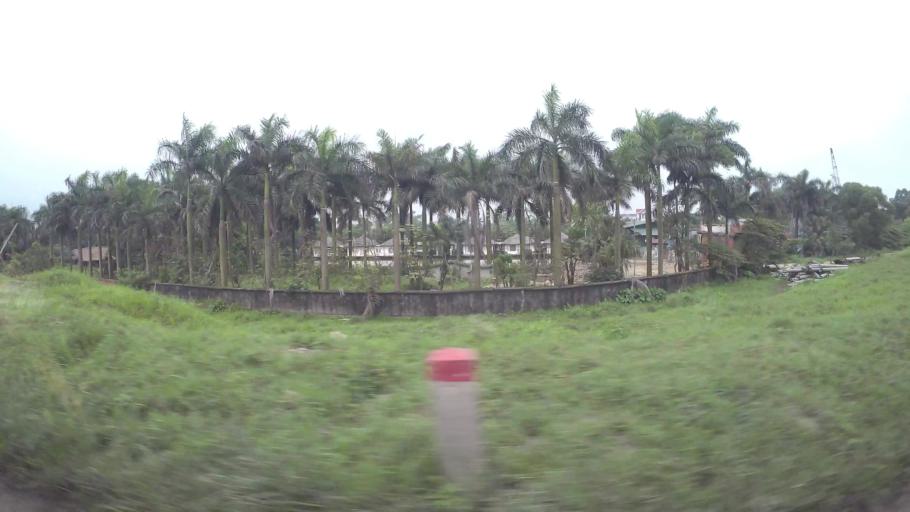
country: VN
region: Ha Noi
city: Trau Quy
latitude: 21.0740
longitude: 105.9153
